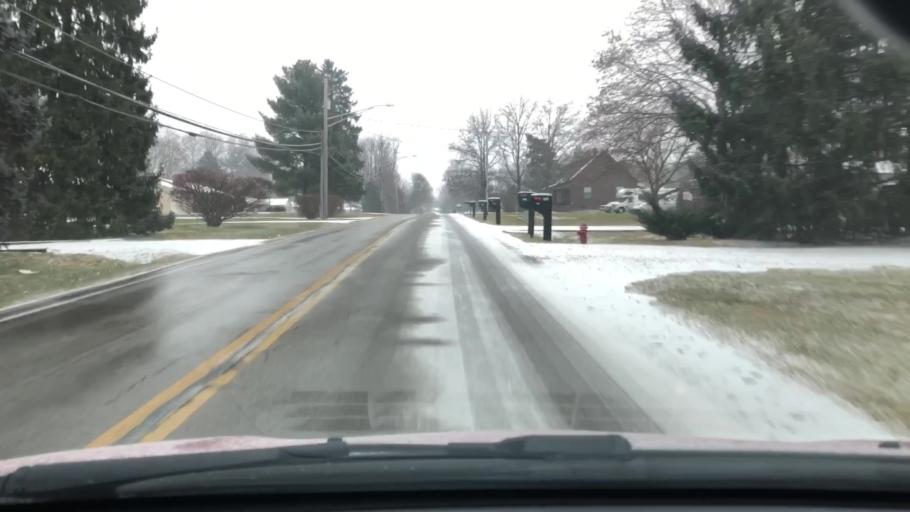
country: US
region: Ohio
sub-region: Franklin County
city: Westerville
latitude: 40.1256
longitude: -82.9097
